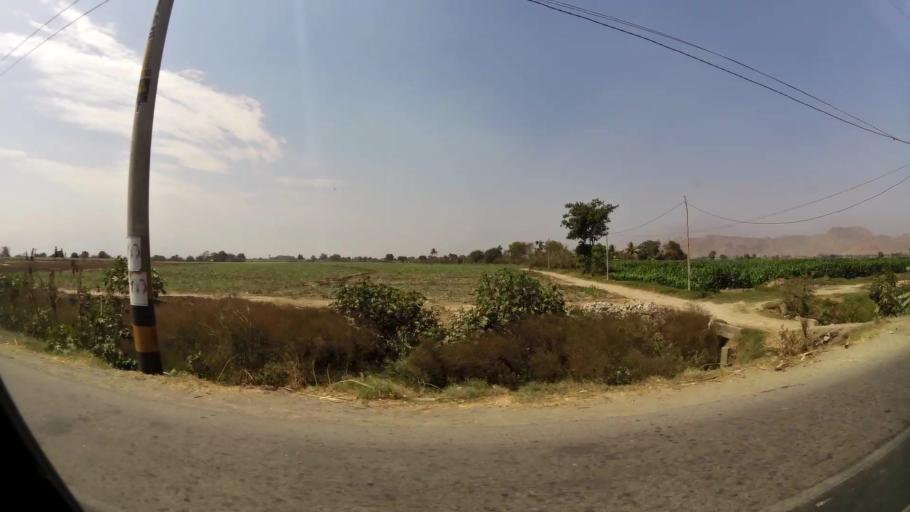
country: PE
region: La Libertad
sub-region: Chepen
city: Chepen
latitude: -7.1933
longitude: -79.4296
